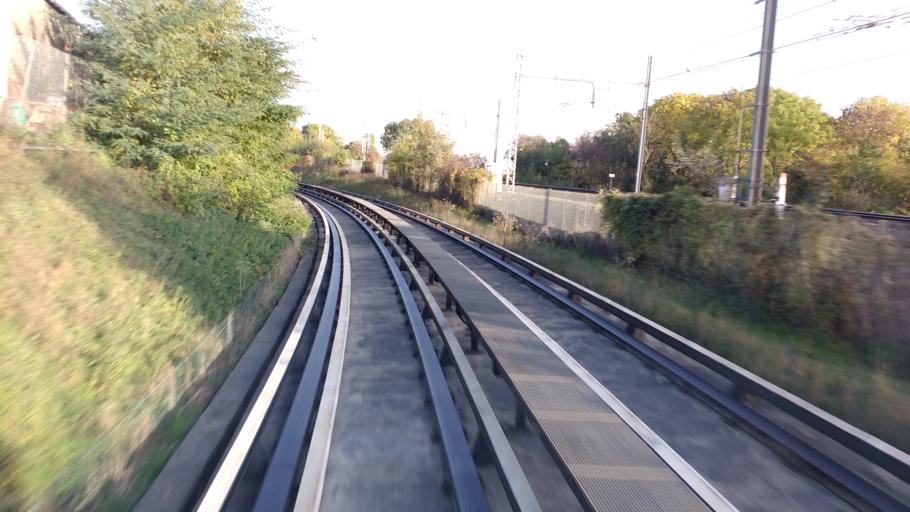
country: FR
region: Ile-de-France
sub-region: Departement du Val-de-Marne
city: Rungis
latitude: 48.7389
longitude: 2.3389
